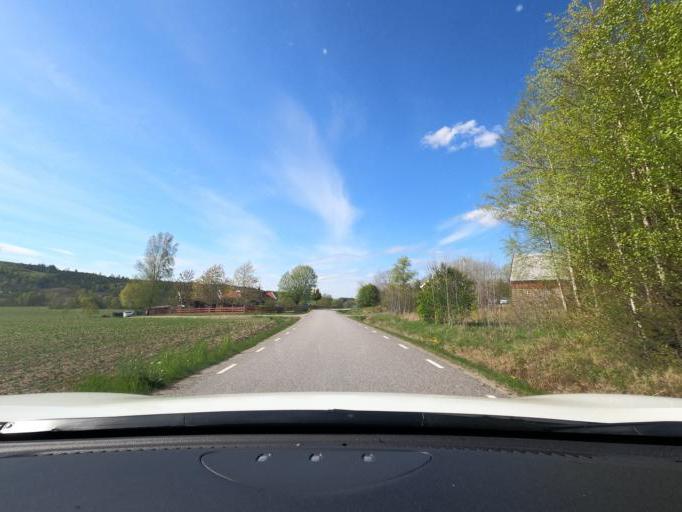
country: SE
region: Vaestra Goetaland
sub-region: Harryda Kommun
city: Ravlanda
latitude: 57.6169
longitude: 12.4958
